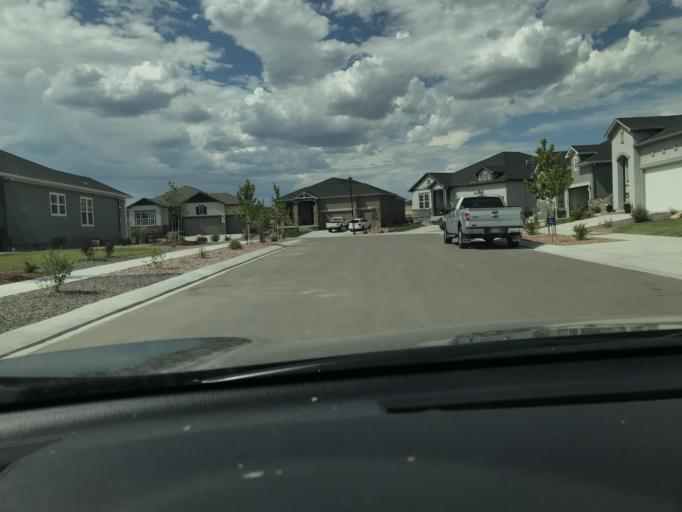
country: US
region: Colorado
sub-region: El Paso County
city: Black Forest
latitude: 38.9646
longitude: -104.7025
